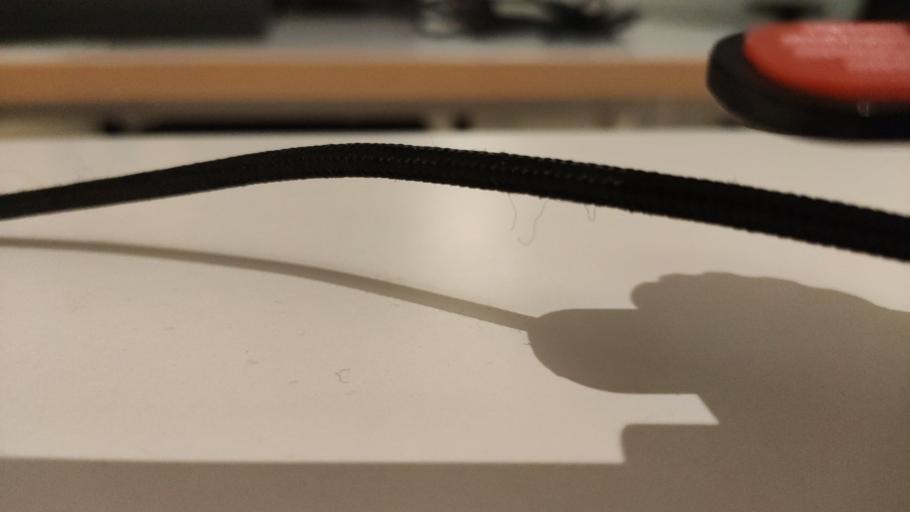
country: RU
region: Moskovskaya
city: Budenovetc
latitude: 56.3976
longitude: 37.6373
